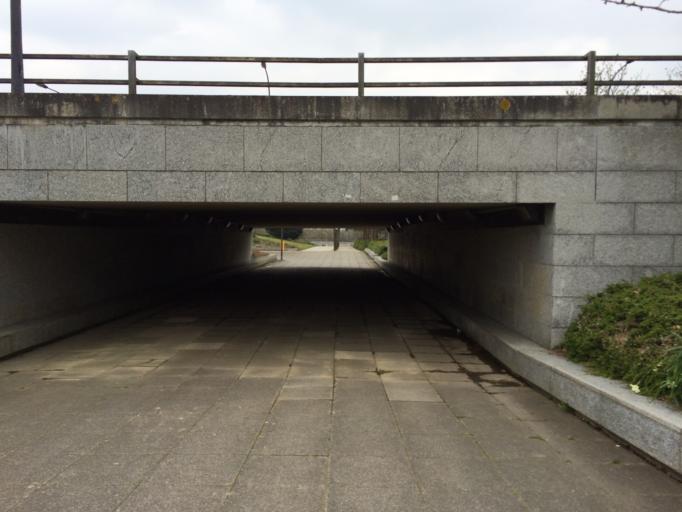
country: GB
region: England
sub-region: Milton Keynes
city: Milton Keynes
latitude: 52.0347
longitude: -0.7684
